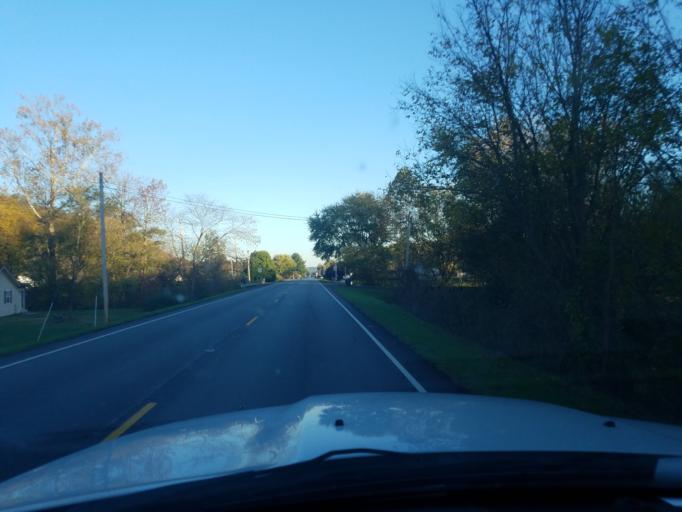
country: US
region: Indiana
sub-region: Washington County
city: New Pekin
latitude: 38.4707
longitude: -85.9585
